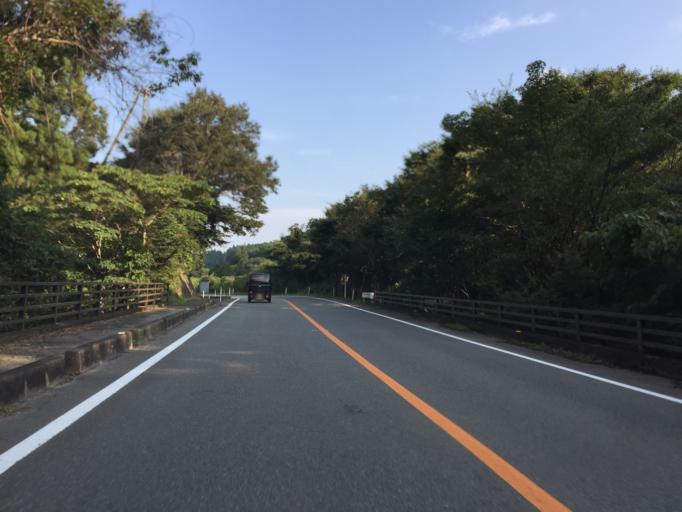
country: JP
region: Fukushima
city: Namie
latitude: 37.5073
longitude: 140.9218
